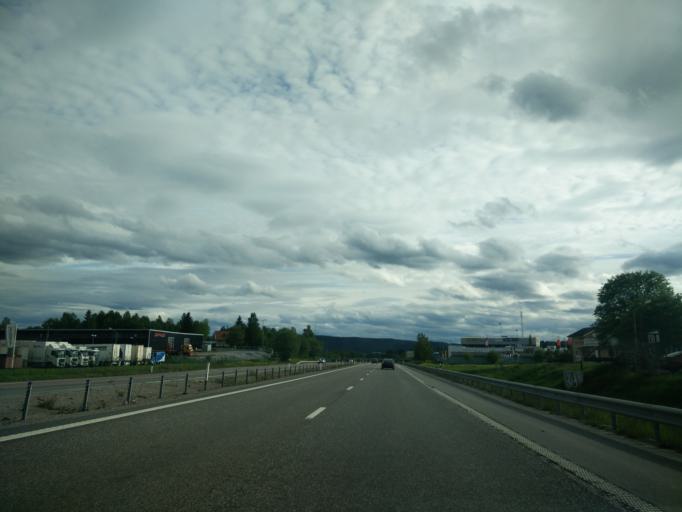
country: SE
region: Vaesternorrland
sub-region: Sundsvalls Kommun
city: Johannedal
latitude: 62.4176
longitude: 17.3448
